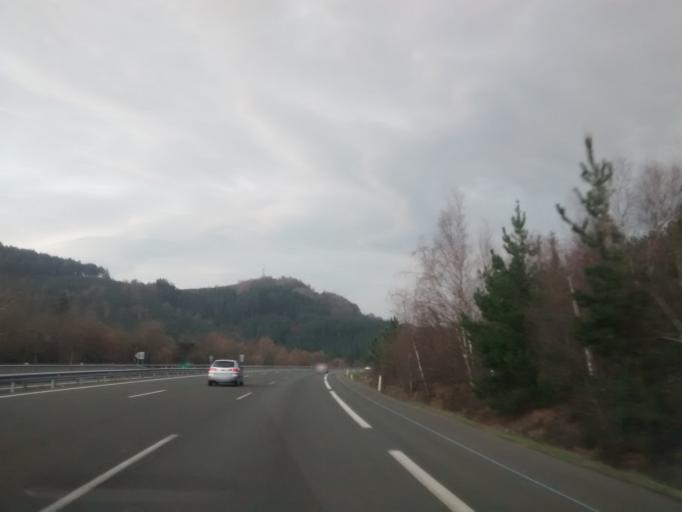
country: ES
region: Basque Country
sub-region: Provincia de Alava
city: Lezama
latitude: 43.0372
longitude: -2.9178
